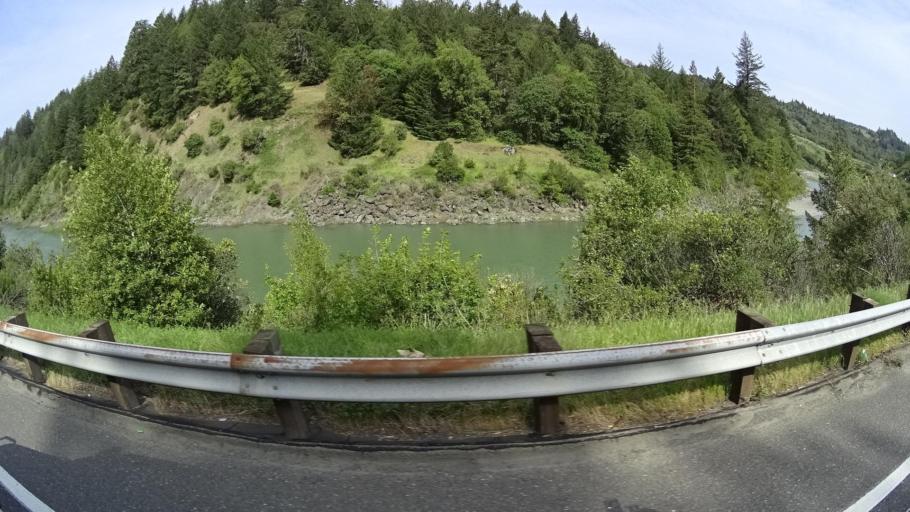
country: US
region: California
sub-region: Humboldt County
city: Redway
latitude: 40.1503
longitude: -123.7958
